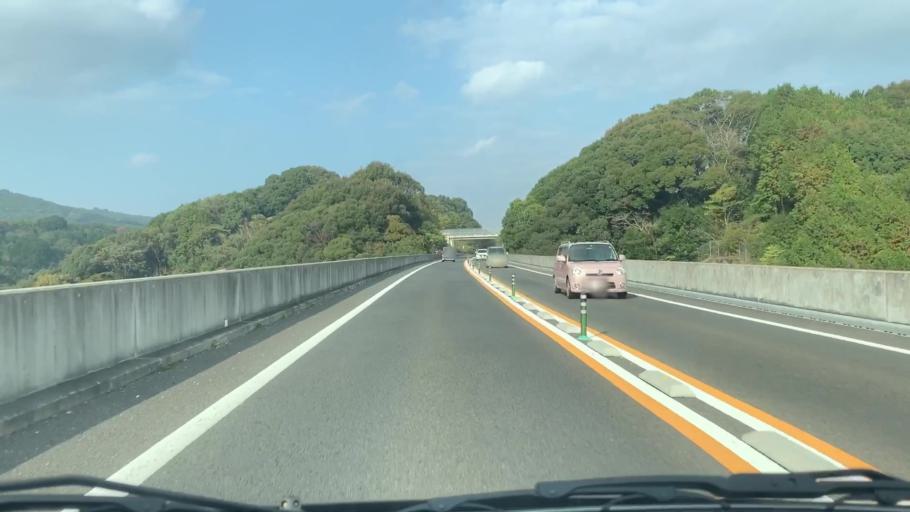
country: JP
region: Nagasaki
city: Sasebo
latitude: 33.0047
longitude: 129.7273
